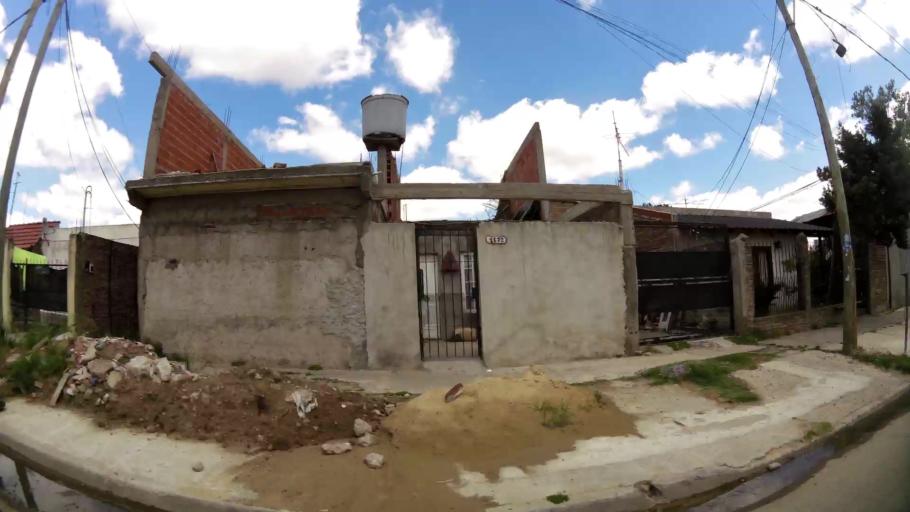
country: AR
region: Buenos Aires
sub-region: Partido de Lanus
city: Lanus
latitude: -34.7107
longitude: -58.4302
